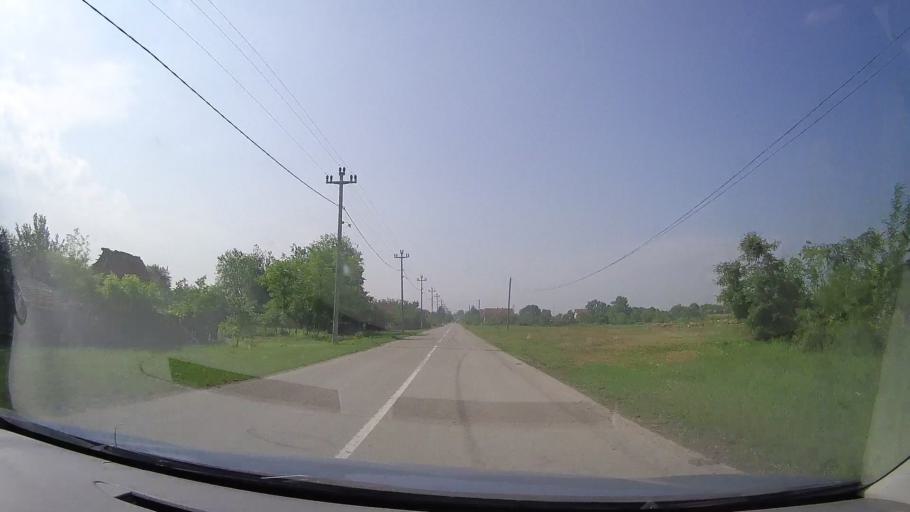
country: RS
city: Jasa Tomic
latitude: 45.4554
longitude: 20.8555
